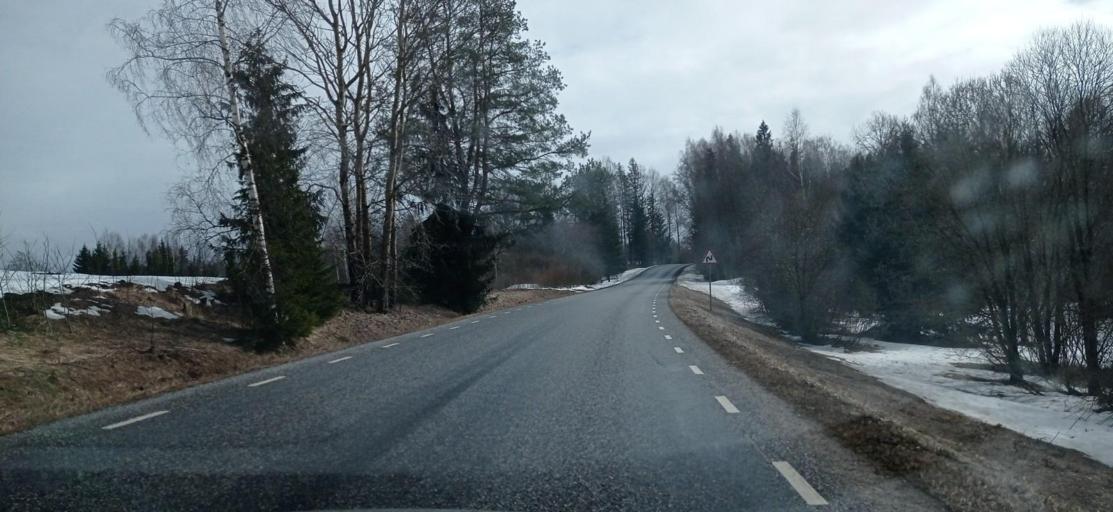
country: EE
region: Tartu
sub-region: UElenurme vald
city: Ulenurme
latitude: 58.0812
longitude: 26.6785
